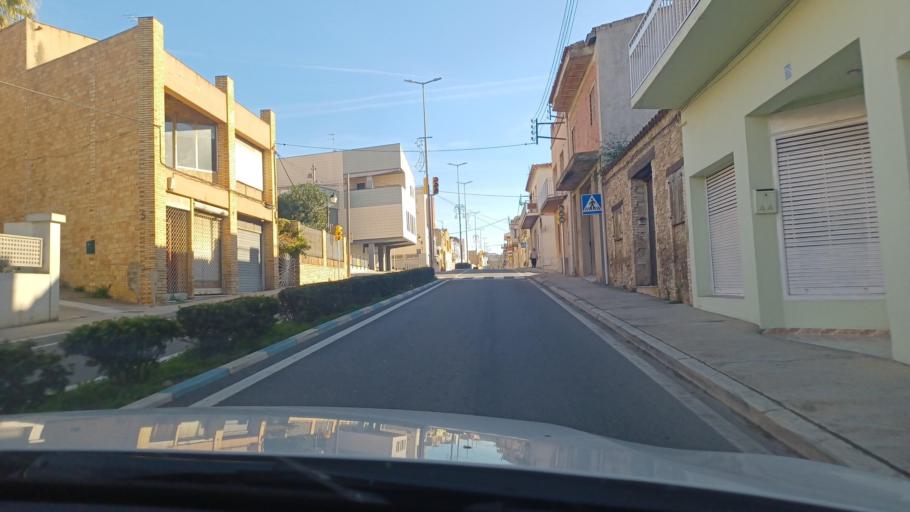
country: ES
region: Catalonia
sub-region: Provincia de Tarragona
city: Masdenverge
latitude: 40.7150
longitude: 0.5297
